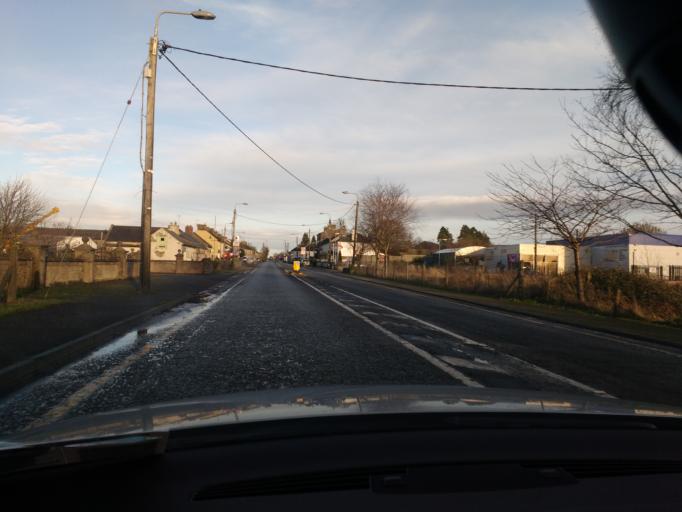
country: IE
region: Munster
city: Thurles
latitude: 52.6381
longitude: -7.7405
